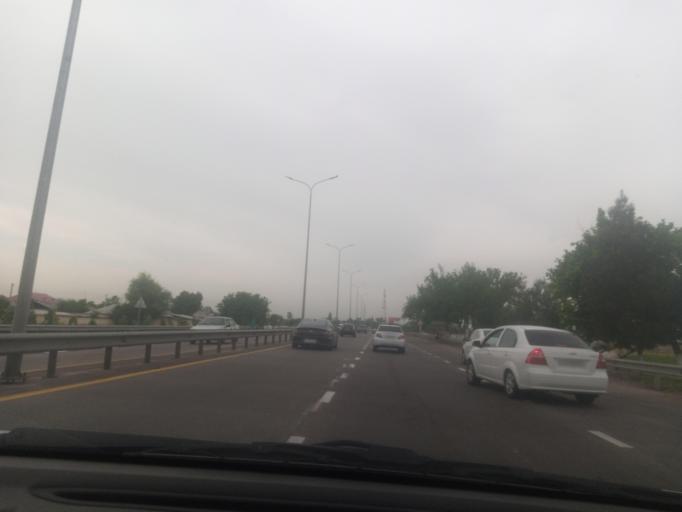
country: UZ
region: Toshkent
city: Tuytepa
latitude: 41.1300
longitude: 69.4365
